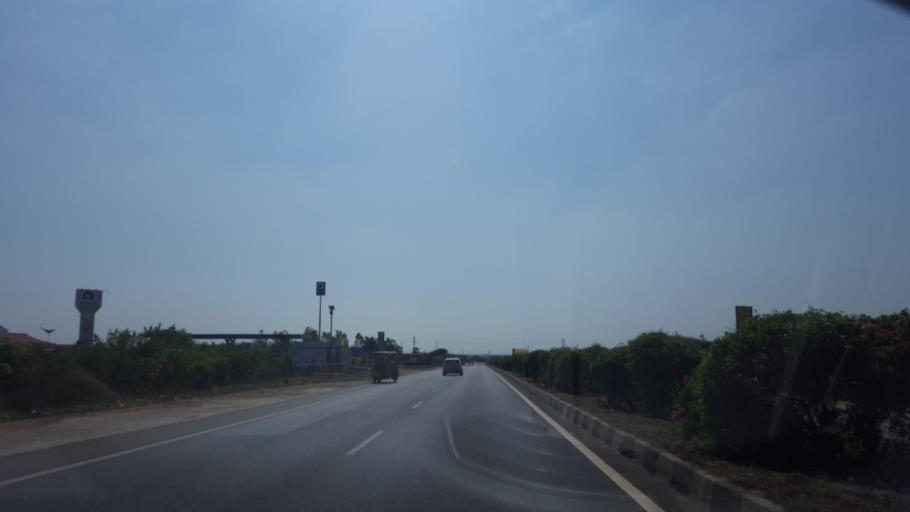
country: IN
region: Andhra Pradesh
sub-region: Nellore
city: Vadlapudi
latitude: 14.3025
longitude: 79.9109
